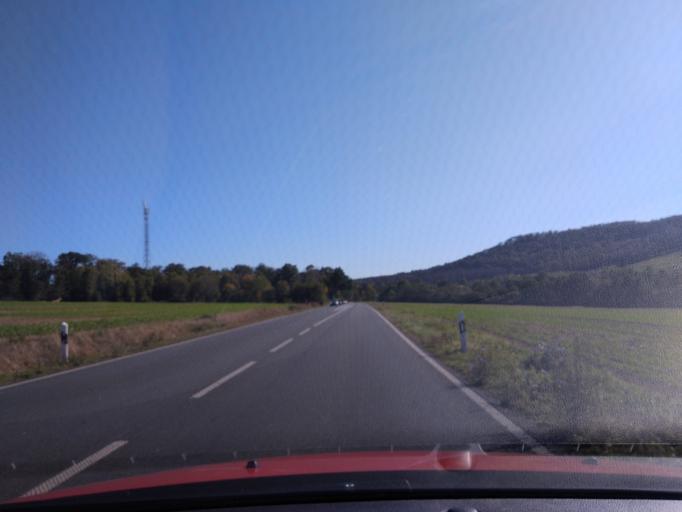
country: DE
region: Lower Saxony
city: Furstenberg
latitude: 51.7180
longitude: 9.3732
